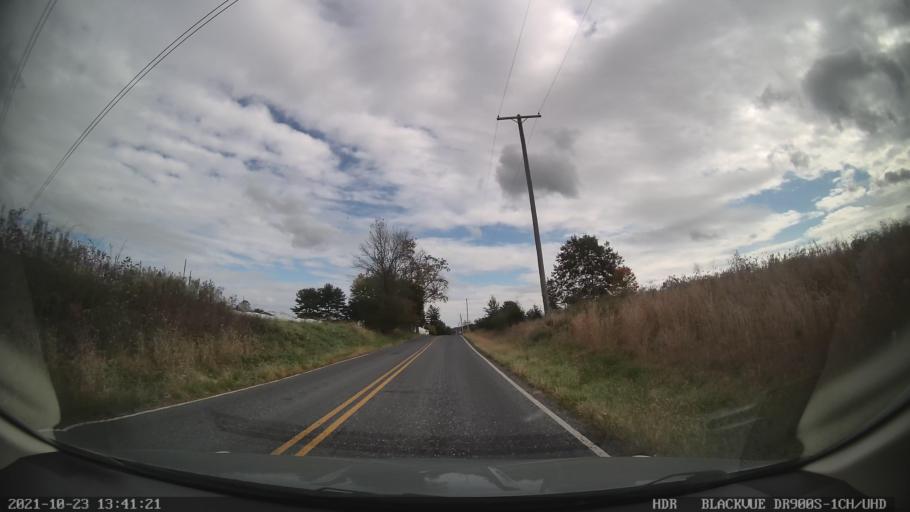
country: US
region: Pennsylvania
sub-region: Berks County
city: Bally
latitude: 40.4137
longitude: -75.5659
